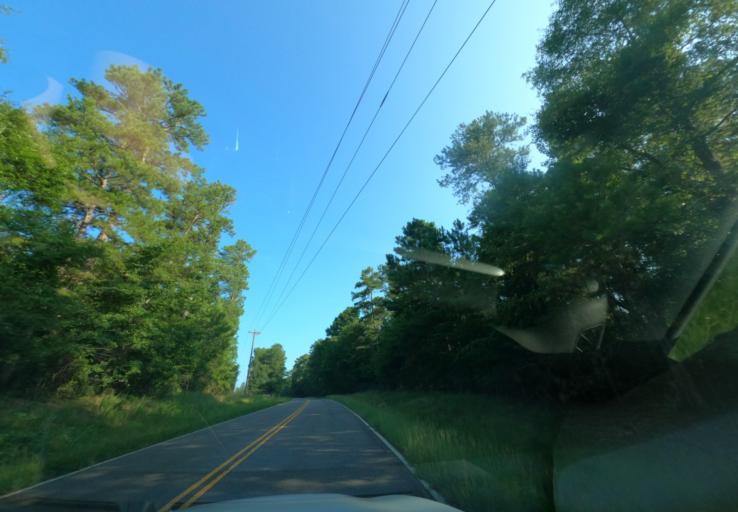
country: US
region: South Carolina
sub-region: Edgefield County
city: Murphys Estates
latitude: 33.6750
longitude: -81.9794
